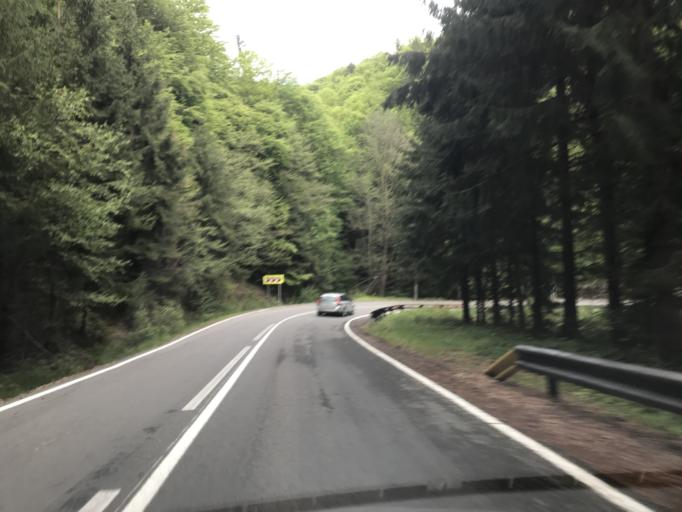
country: RO
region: Sibiu
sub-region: Comuna Cartisoara
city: Cartisoara
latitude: 45.6759
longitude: 24.5848
